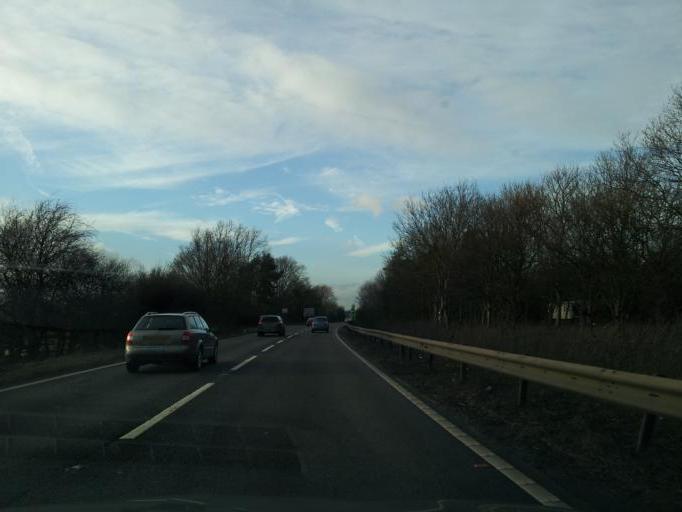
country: GB
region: England
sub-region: Peterborough
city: Castor
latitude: 52.5416
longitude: -0.3280
